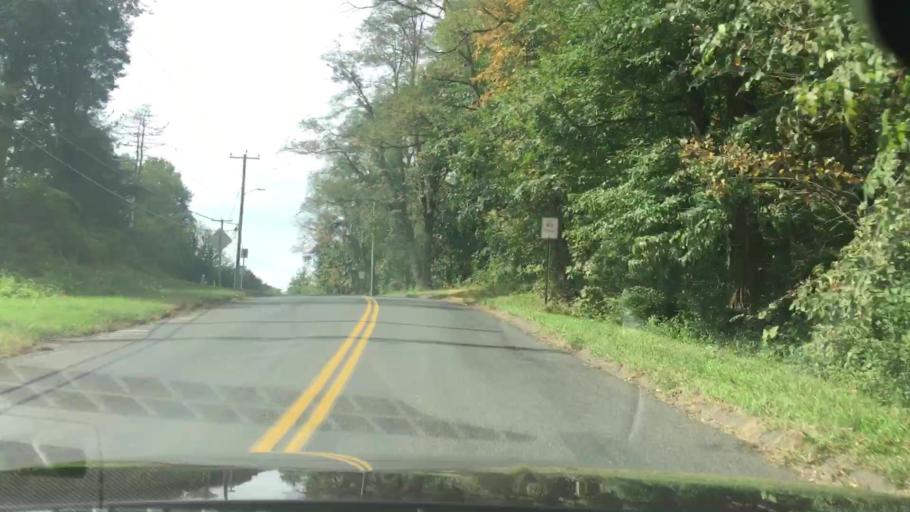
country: US
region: Connecticut
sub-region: Hartford County
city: South Windsor
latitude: 41.8599
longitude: -72.5826
